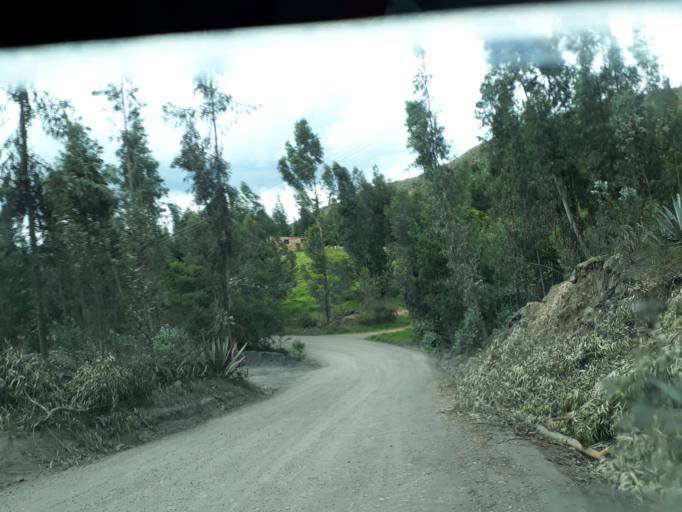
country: CO
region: Cundinamarca
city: Cucunuba
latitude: 5.2388
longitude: -73.7980
